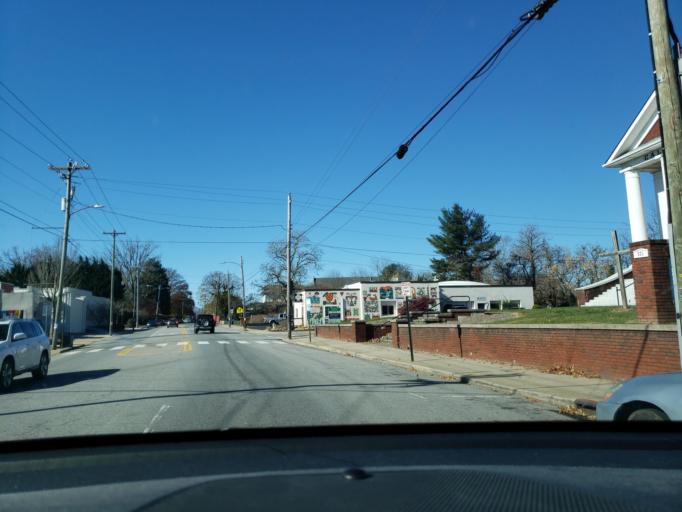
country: US
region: North Carolina
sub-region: Buncombe County
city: Asheville
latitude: 35.5786
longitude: -82.5849
